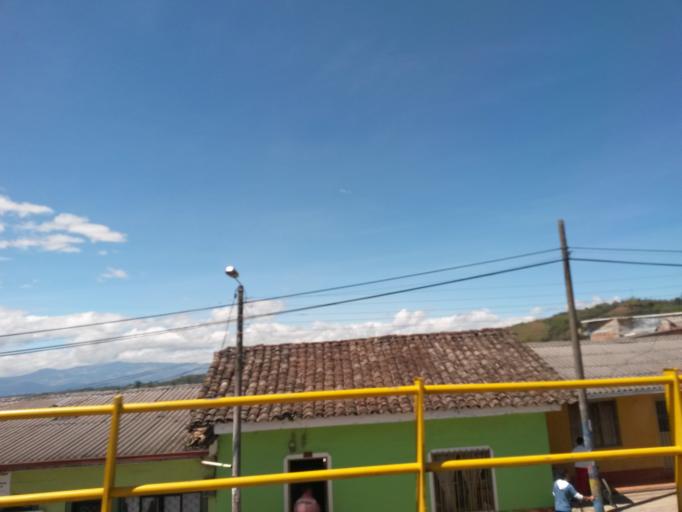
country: CO
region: Cauca
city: El Tambo
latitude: 2.4508
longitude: -76.8133
